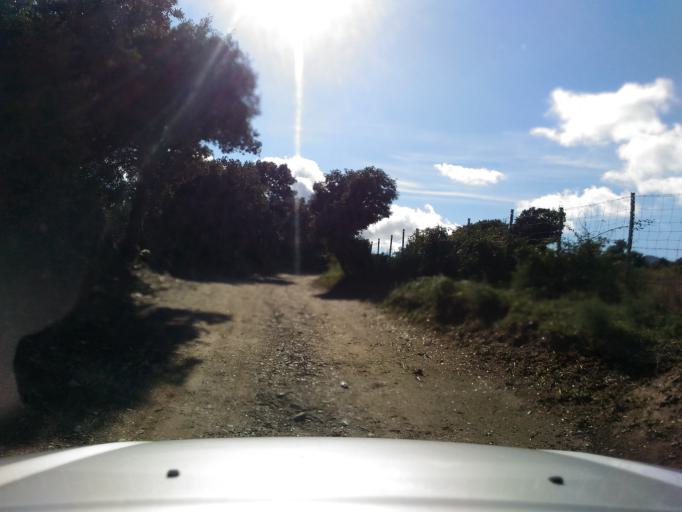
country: FR
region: Corsica
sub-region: Departement de la Haute-Corse
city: Brando
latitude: 42.9683
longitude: 9.4509
